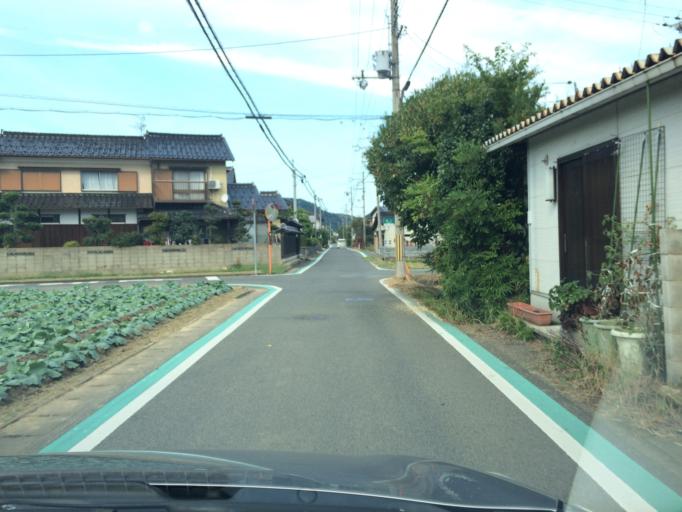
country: JP
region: Hyogo
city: Toyooka
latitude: 35.4935
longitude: 134.8031
